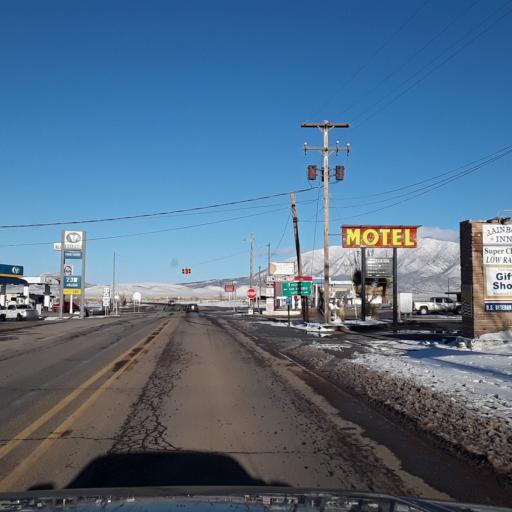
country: US
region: New Mexico
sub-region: Lincoln County
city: Carrizozo
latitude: 33.6456
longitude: -105.8722
